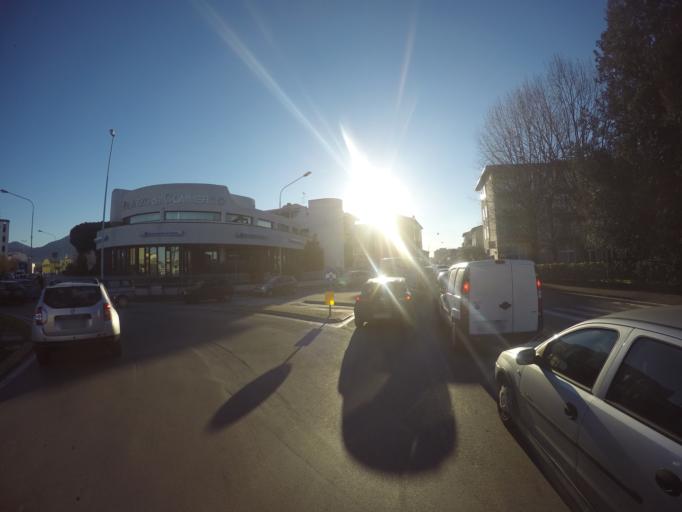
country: IT
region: Tuscany
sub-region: Provincia di Prato
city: Prato
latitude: 43.8774
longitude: 11.0803
